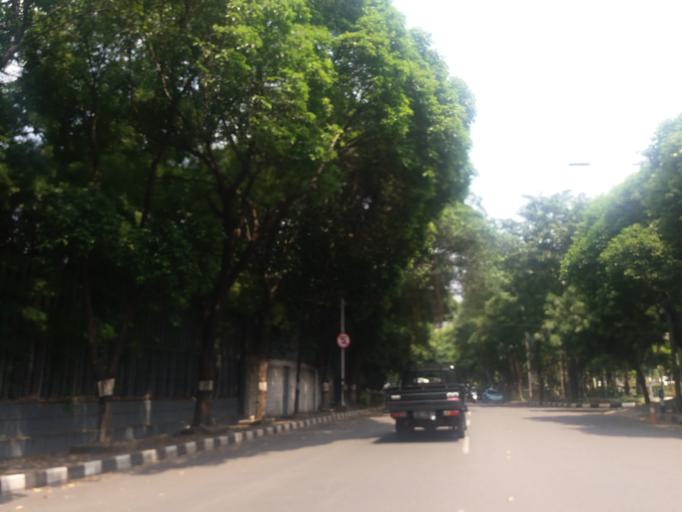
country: ID
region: Jakarta Raya
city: Jakarta
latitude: -6.2342
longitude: 106.8278
